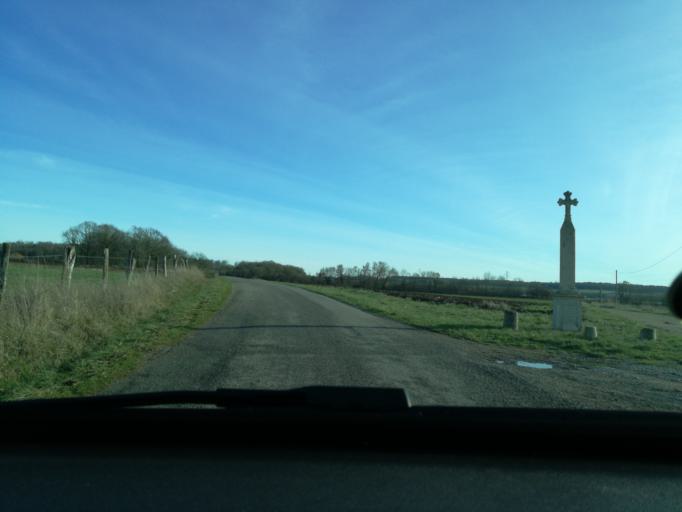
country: FR
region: Lorraine
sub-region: Departement de la Meuse
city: Revigny-sur-Ornain
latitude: 48.8188
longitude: 5.0585
